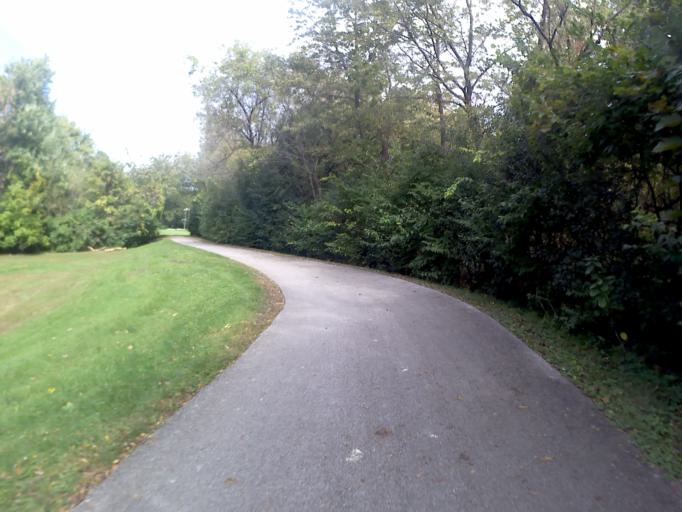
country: US
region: Illinois
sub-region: Kane County
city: Batavia
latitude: 41.8390
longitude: -88.3075
